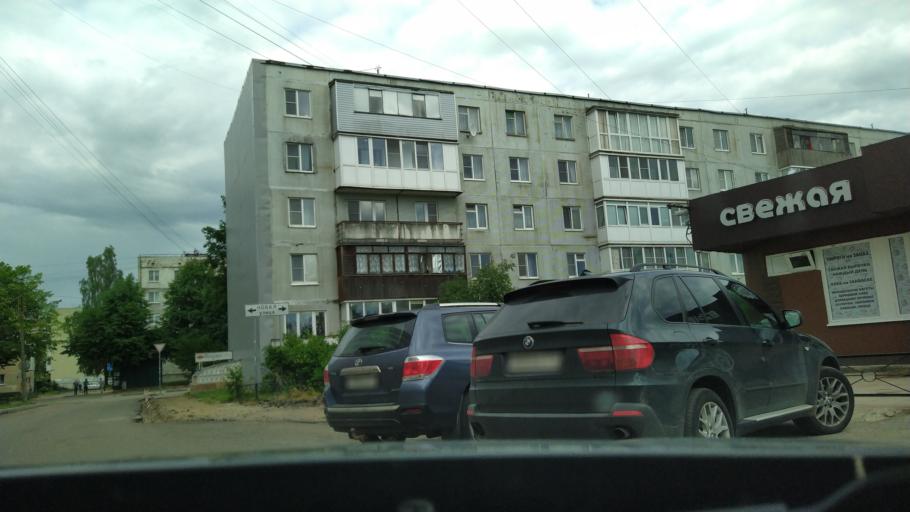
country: RU
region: Leningrad
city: Kirovsk
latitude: 59.8802
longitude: 30.9905
